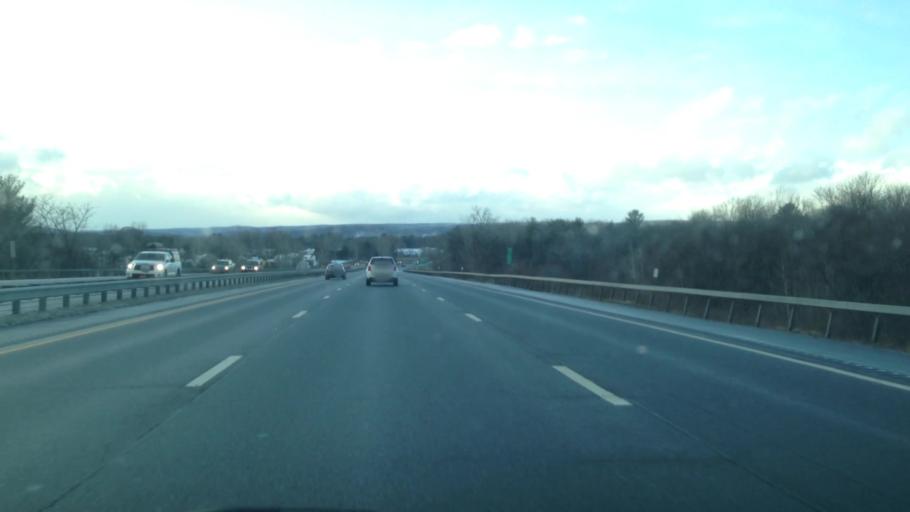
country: US
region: New York
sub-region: Schenectady County
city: Rotterdam
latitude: 42.7749
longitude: -73.9878
